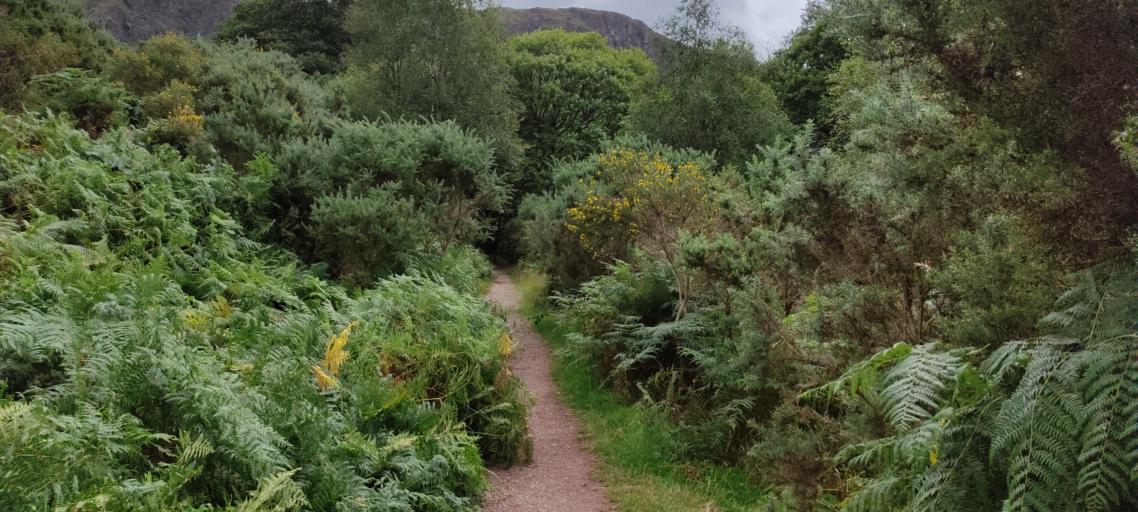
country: GB
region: England
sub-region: Cumbria
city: Millom
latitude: 54.3907
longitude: -3.2669
